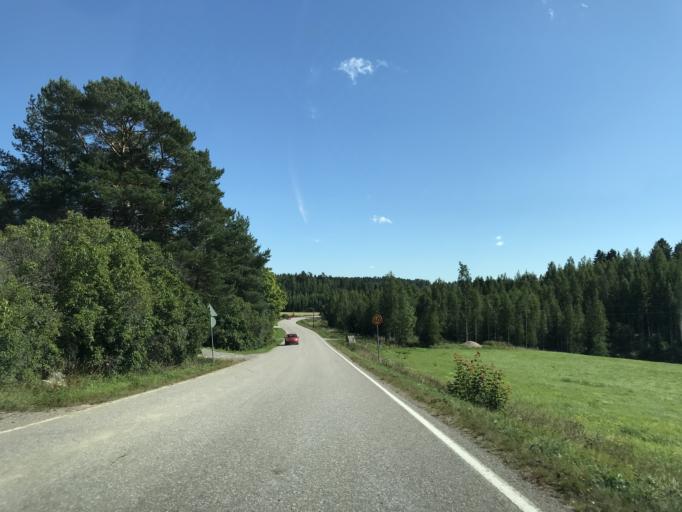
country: FI
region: Paijanne Tavastia
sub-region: Lahti
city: Orimattila
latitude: 60.8064
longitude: 25.6867
